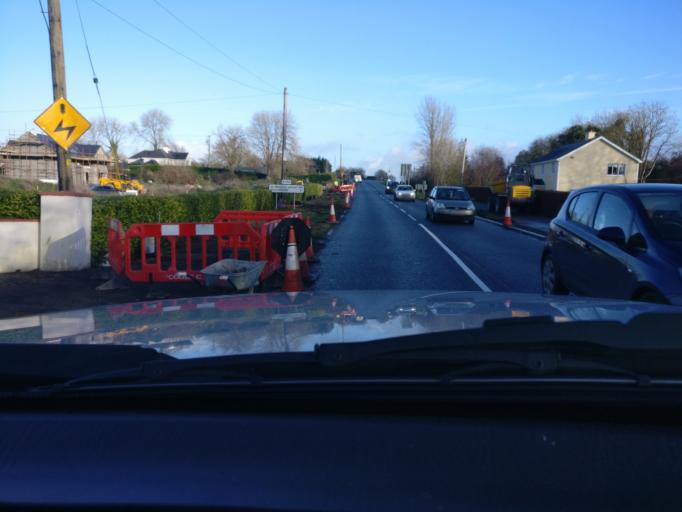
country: IE
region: Leinster
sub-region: An Iarmhi
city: An Muileann gCearr
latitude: 53.5071
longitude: -7.4202
